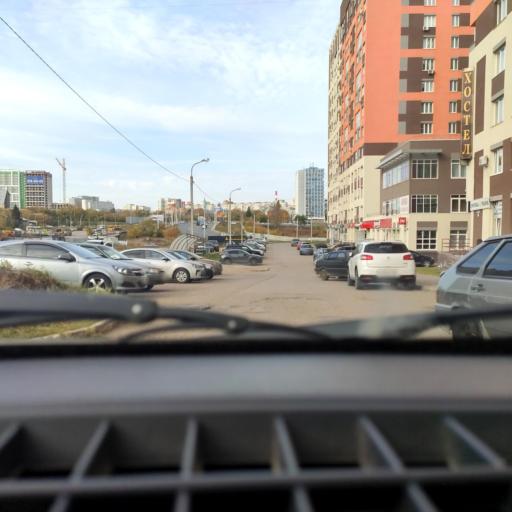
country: RU
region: Bashkortostan
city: Ufa
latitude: 54.7170
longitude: 55.9798
